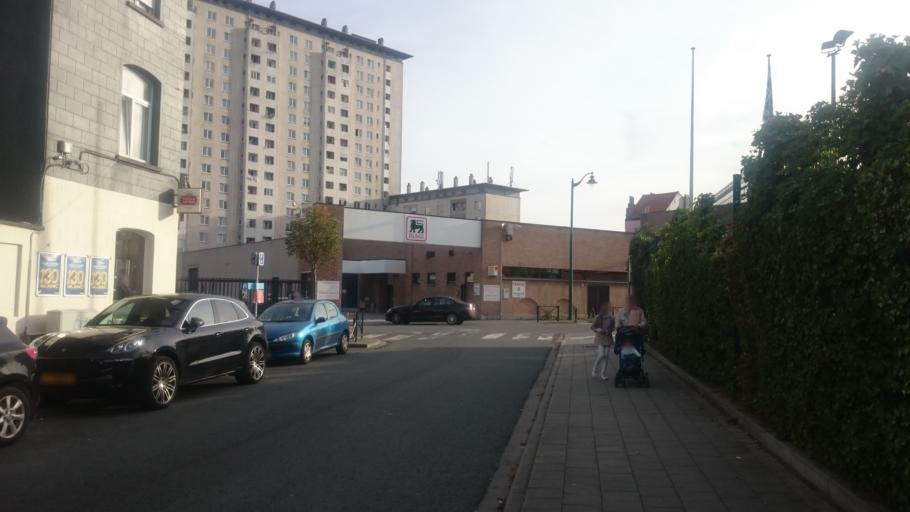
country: BE
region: Brussels Capital
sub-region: Bruxelles-Capitale
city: Brussels
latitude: 50.8557
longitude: 4.3218
